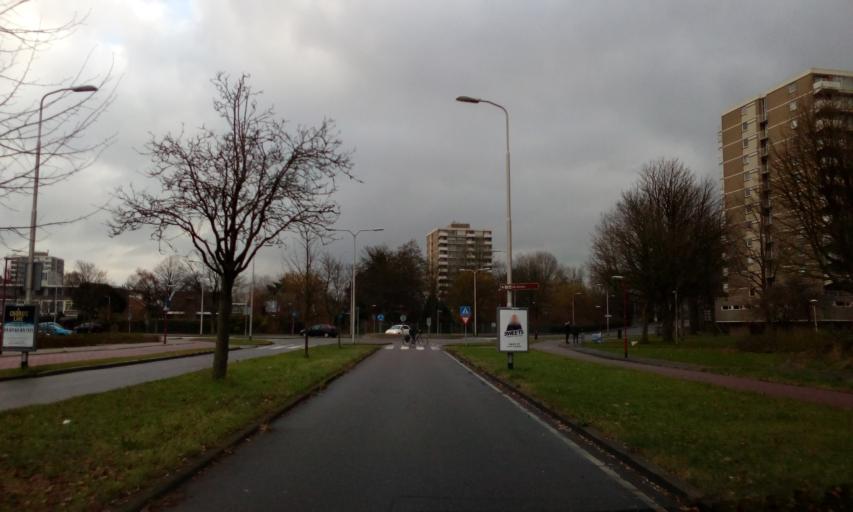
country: NL
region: South Holland
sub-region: Gemeente Zoetermeer
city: Zoetermeer
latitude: 52.0526
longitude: 4.4838
